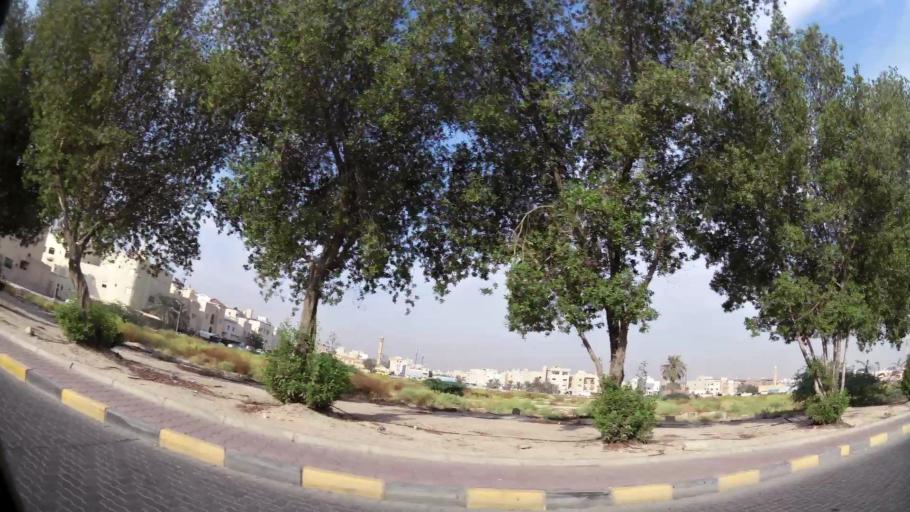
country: KW
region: Muhafazat Hawalli
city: Salwa
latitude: 29.3036
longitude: 48.0852
